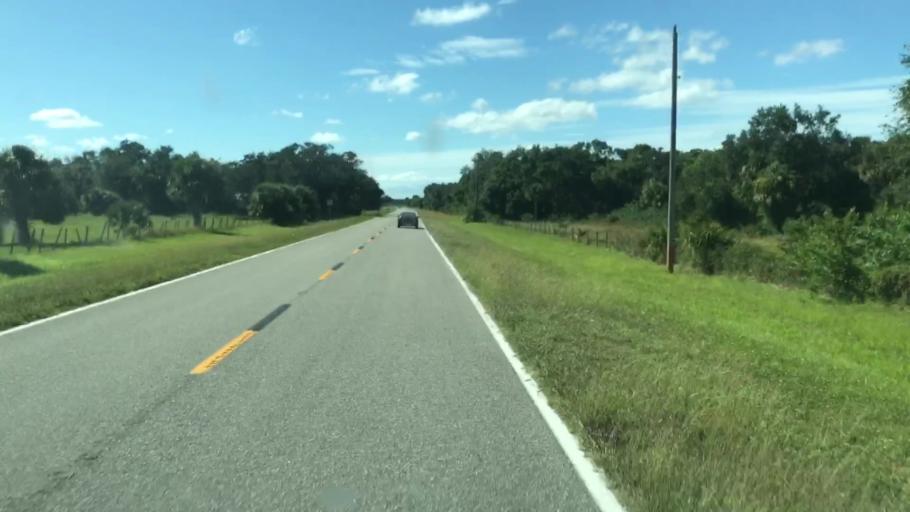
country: US
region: Florida
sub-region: Lee County
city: Olga
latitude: 26.7400
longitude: -81.7335
